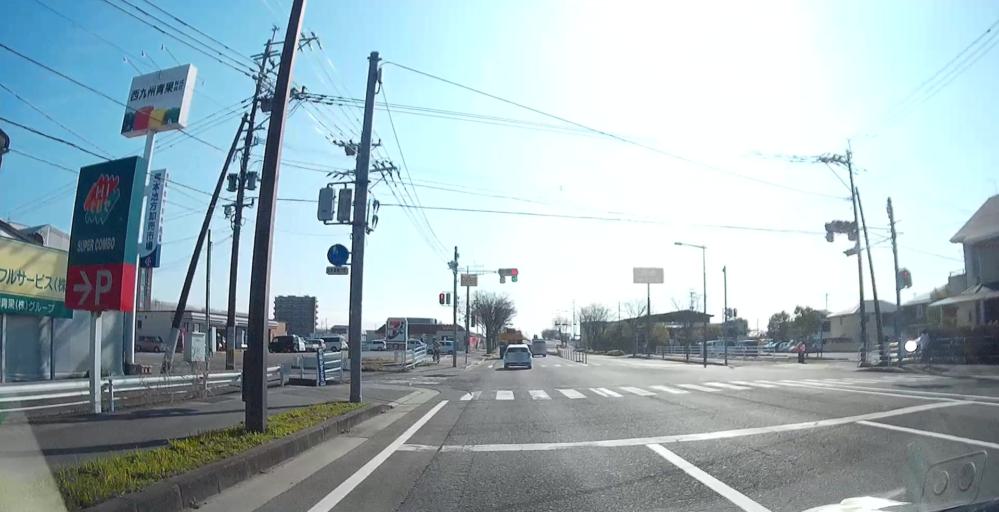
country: JP
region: Kumamoto
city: Kumamoto
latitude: 32.7819
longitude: 130.6734
